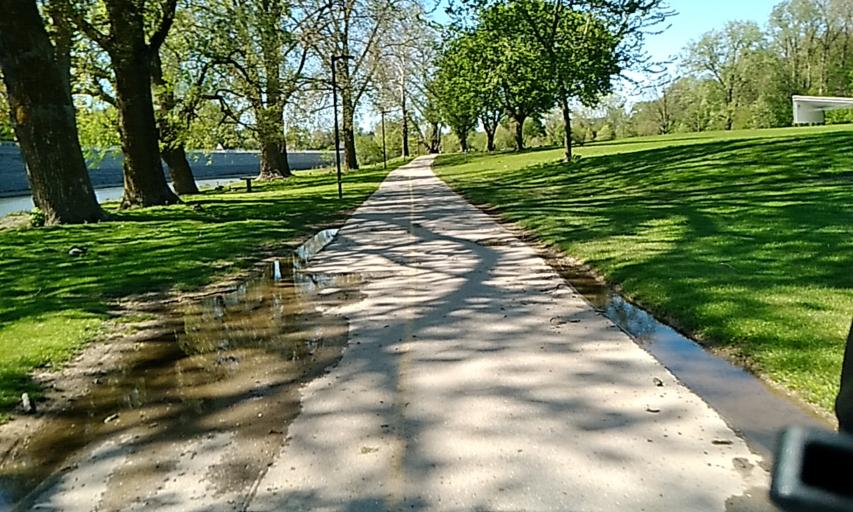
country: CA
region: Ontario
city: London
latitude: 42.9843
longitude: -81.2569
